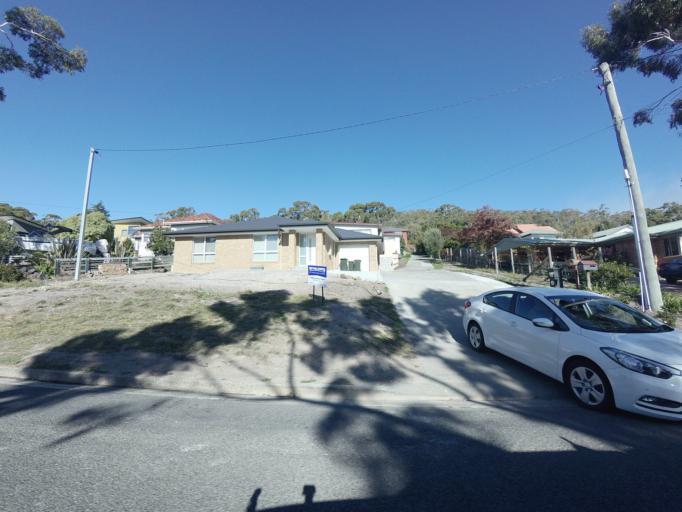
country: AU
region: Tasmania
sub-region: Clarence
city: Lindisfarne
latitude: -42.8412
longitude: 147.3442
